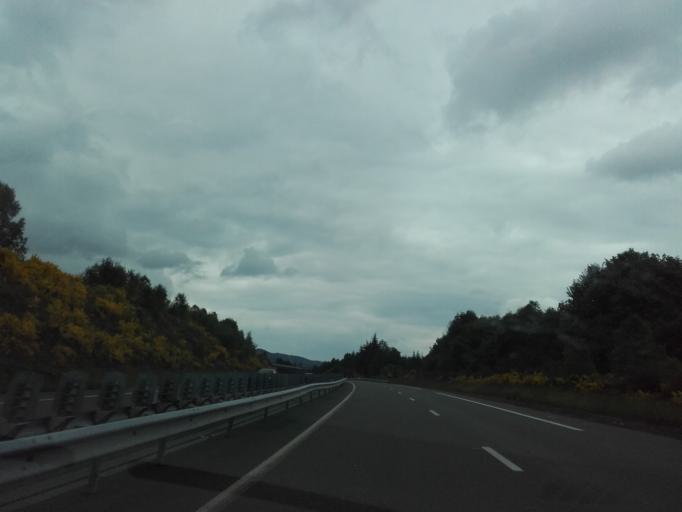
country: FR
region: Limousin
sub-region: Departement de la Correze
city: Egletons
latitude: 45.4185
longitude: 2.0369
